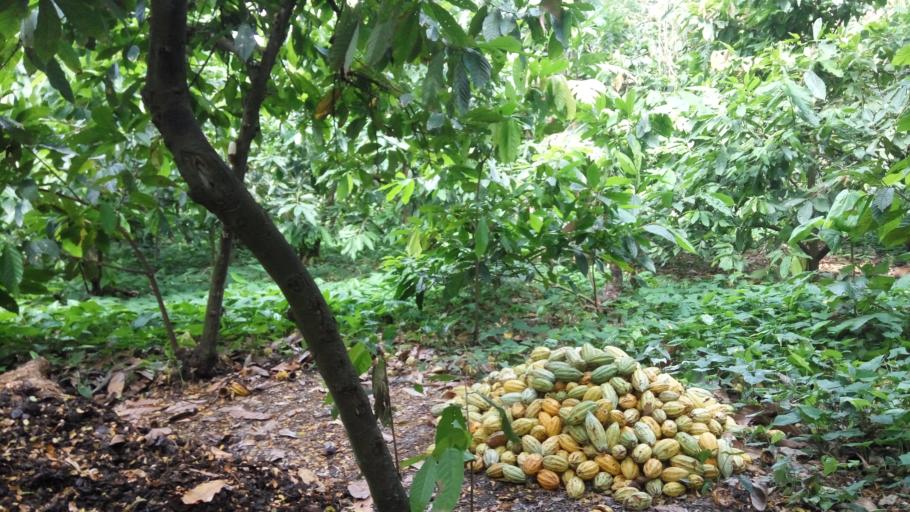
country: MX
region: Tabasco
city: Comalcalco
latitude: 18.2655
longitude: -93.2293
